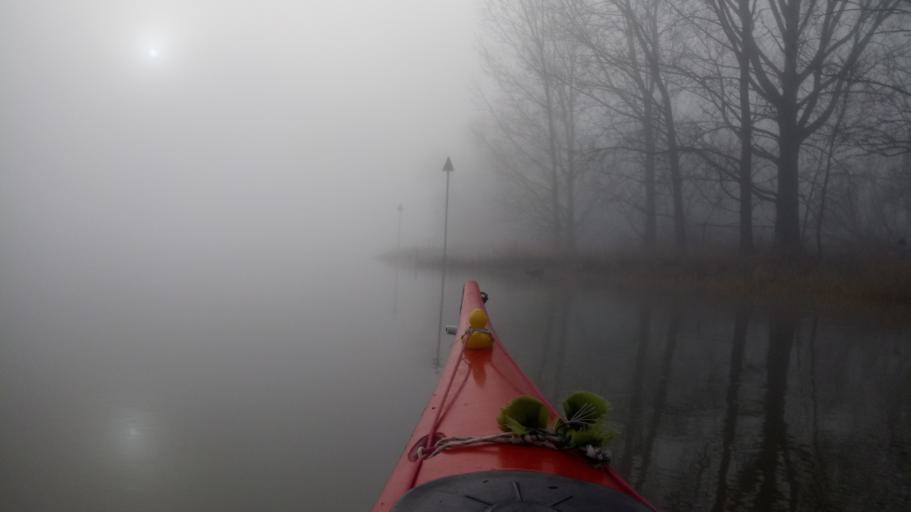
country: NL
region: Gelderland
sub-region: Gemeente Brummen
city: Brummen
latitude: 52.0668
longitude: 6.1494
